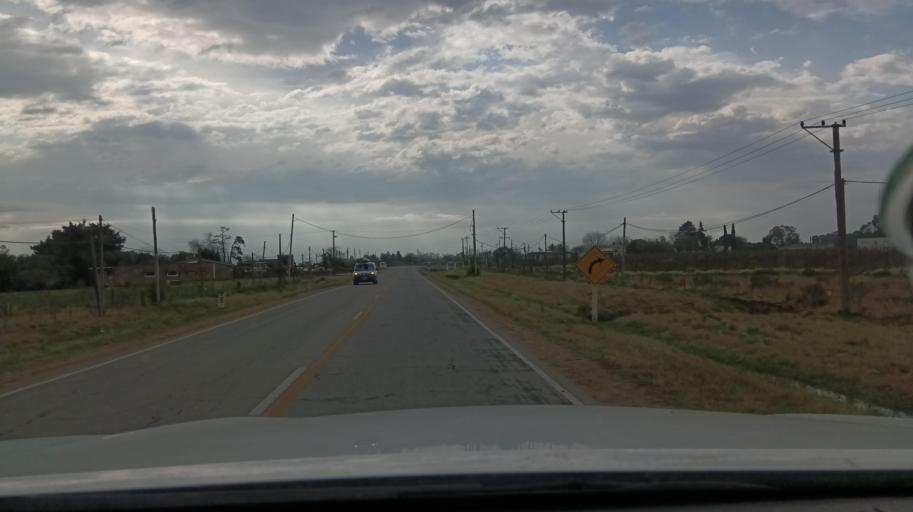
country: UY
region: Canelones
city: Toledo
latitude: -34.7186
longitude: -56.1133
